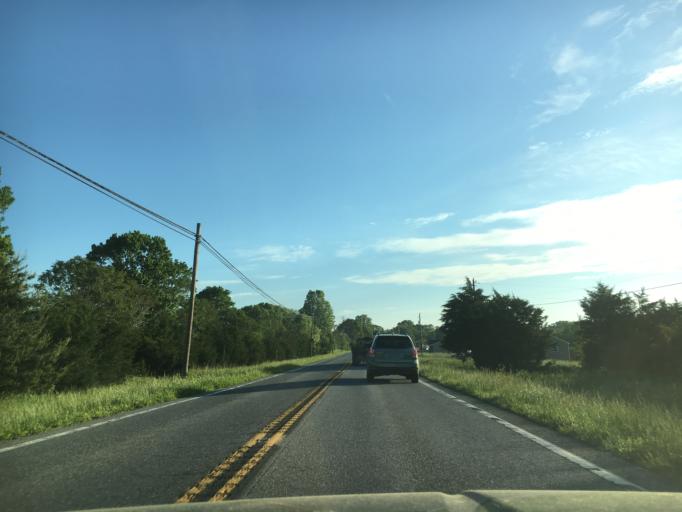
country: US
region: Virginia
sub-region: Campbell County
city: Rustburg
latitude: 37.2626
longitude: -79.1218
